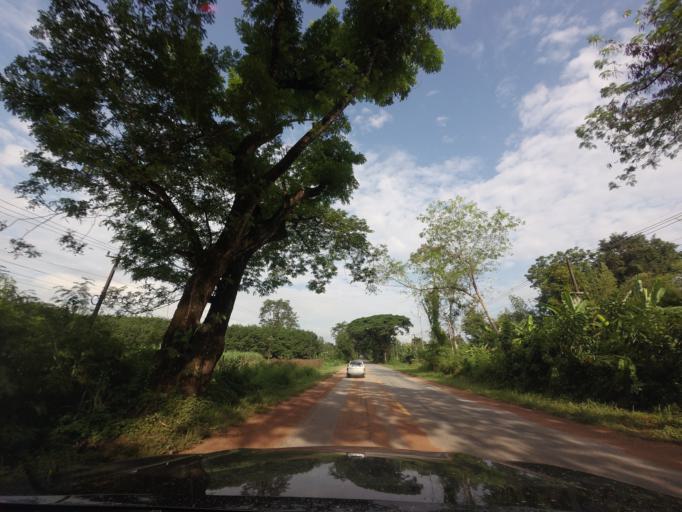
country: TH
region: Nong Khai
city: Pho Tak
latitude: 17.7853
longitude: 102.3709
